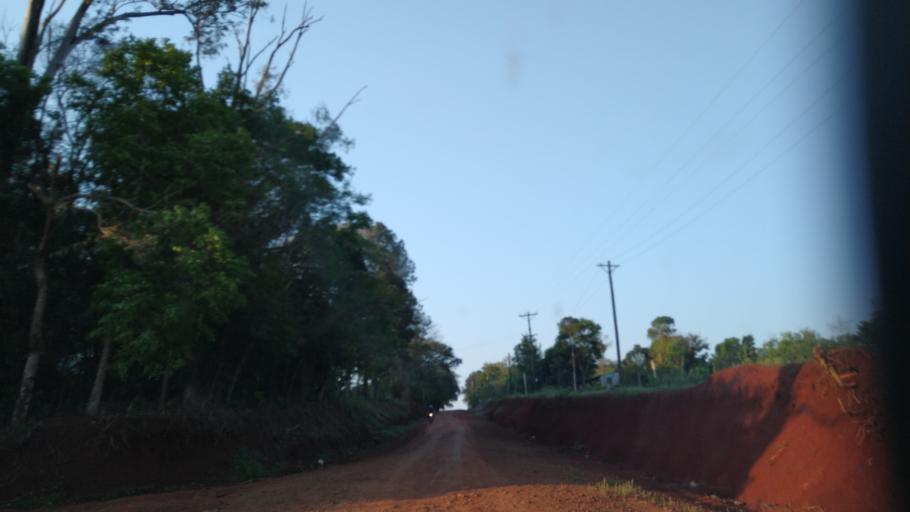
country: AR
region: Misiones
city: Jardin America
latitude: -27.0735
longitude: -55.2696
